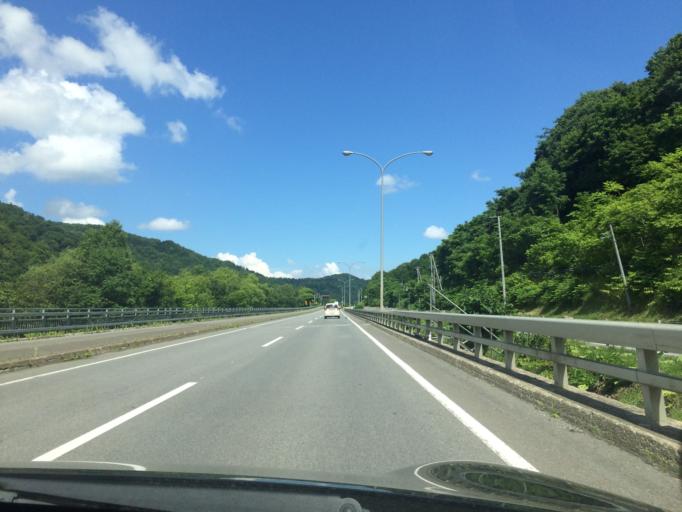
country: JP
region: Hokkaido
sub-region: Asahikawa-shi
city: Asahikawa
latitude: 43.7292
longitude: 142.2229
